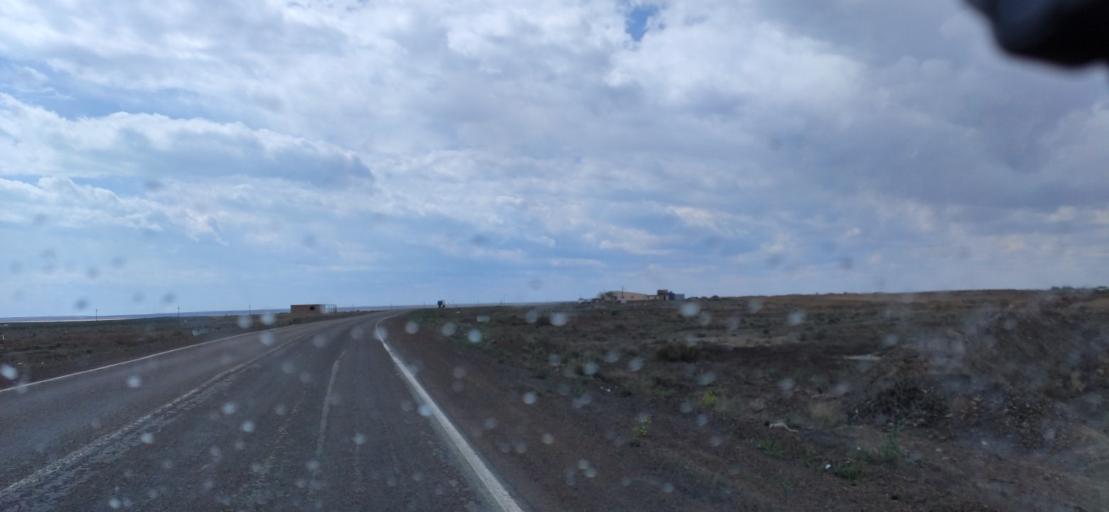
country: KZ
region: Qaraghandy
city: Saryshaghan
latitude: 46.0161
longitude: 73.5915
